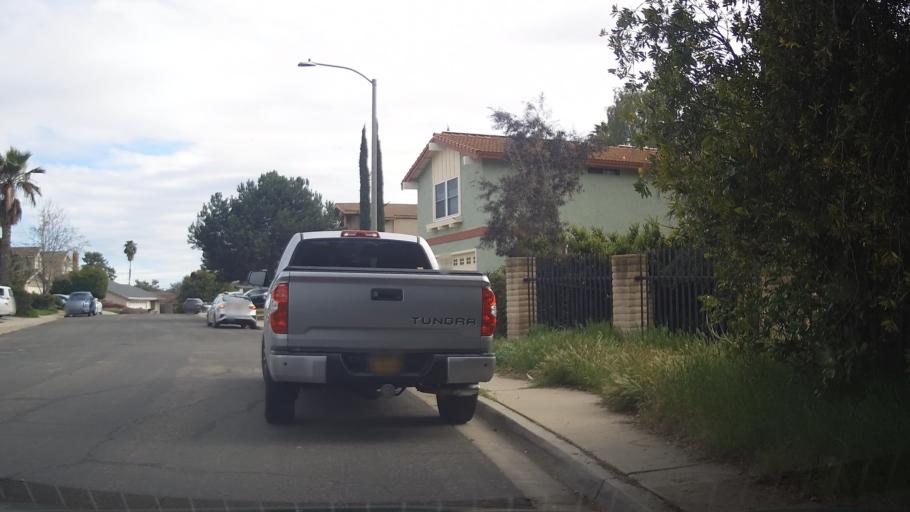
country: US
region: California
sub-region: San Diego County
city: Poway
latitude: 32.9909
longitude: -117.0896
